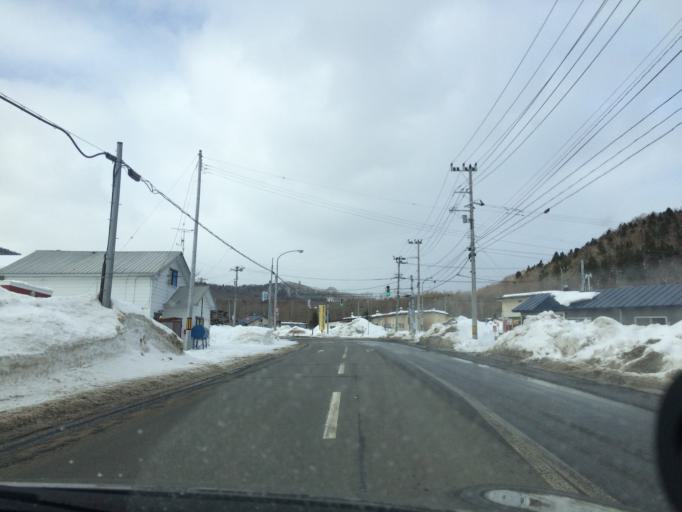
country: JP
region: Hokkaido
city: Shimo-furano
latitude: 43.0048
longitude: 142.4062
